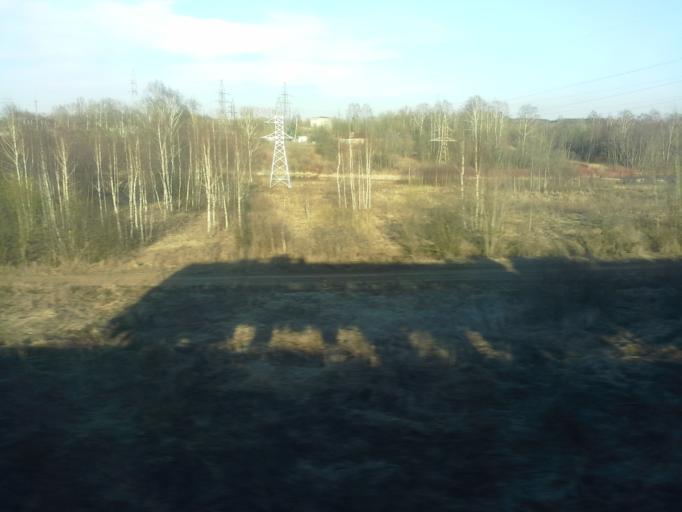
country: RU
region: Moskovskaya
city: Iksha
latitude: 56.1594
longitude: 37.5003
